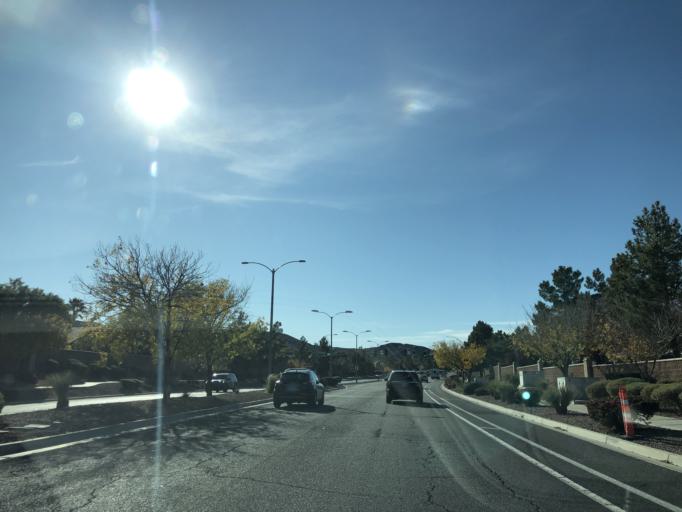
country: US
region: Nevada
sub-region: Clark County
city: Whitney
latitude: 36.0083
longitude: -115.0665
